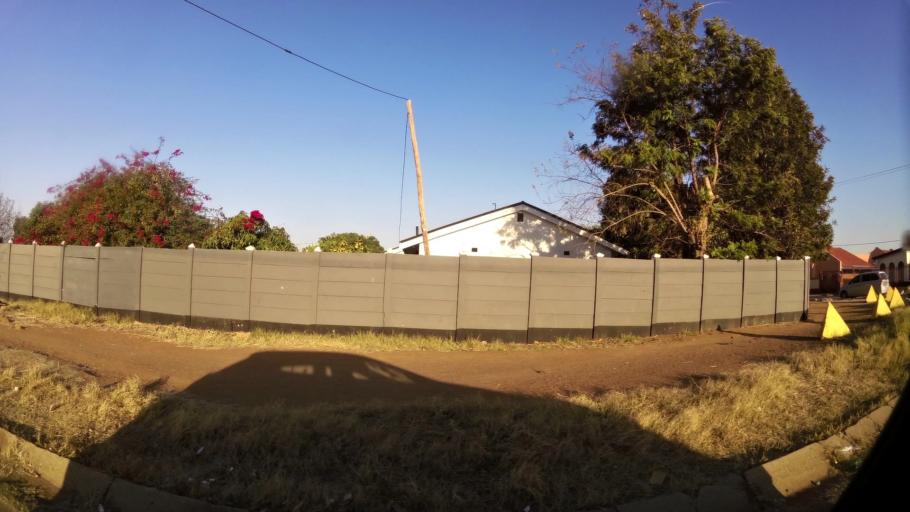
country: ZA
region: North-West
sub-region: Bojanala Platinum District Municipality
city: Rustenburg
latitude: -25.6419
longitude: 27.2102
